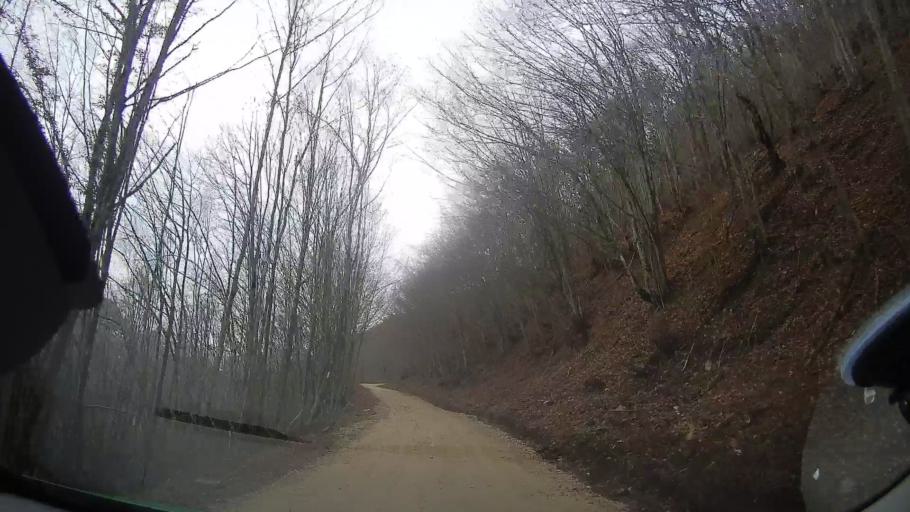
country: RO
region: Cluj
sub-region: Comuna Maguri-Racatau
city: Maguri-Racatau
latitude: 46.6519
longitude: 23.1986
